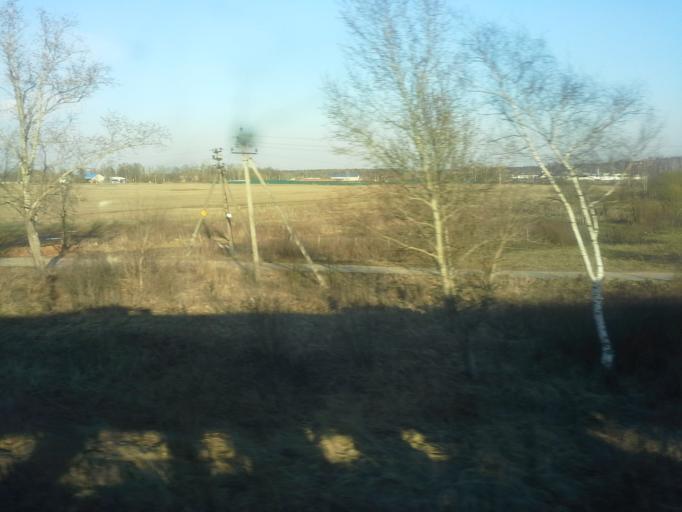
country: RU
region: Moskovskaya
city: Nekrasovskiy
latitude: 56.0820
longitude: 37.5000
